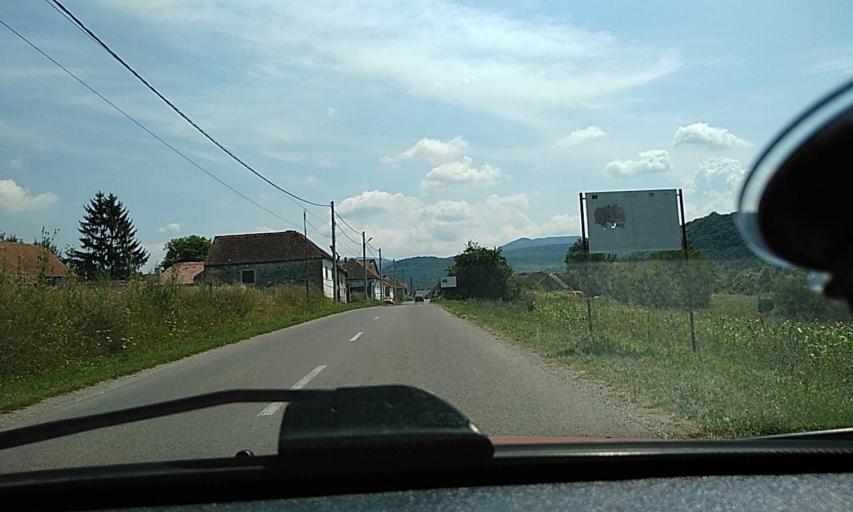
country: RO
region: Brasov
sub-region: Comuna Hoghiz
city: Hoghiz
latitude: 46.0268
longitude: 25.3951
